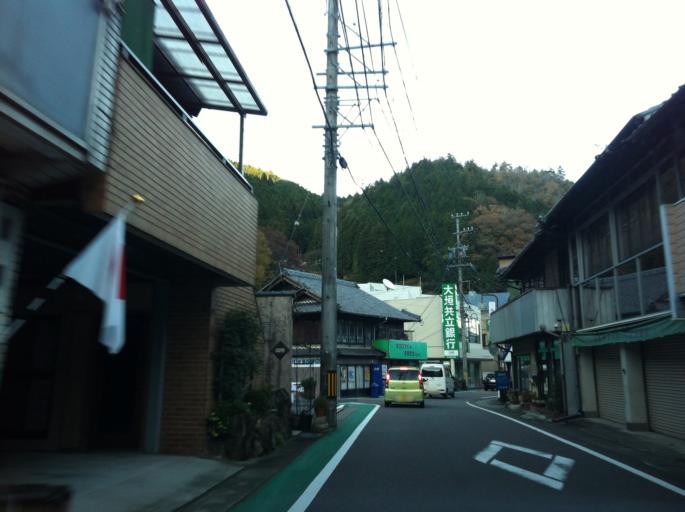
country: JP
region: Gifu
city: Mitake
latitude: 35.5806
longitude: 137.1874
